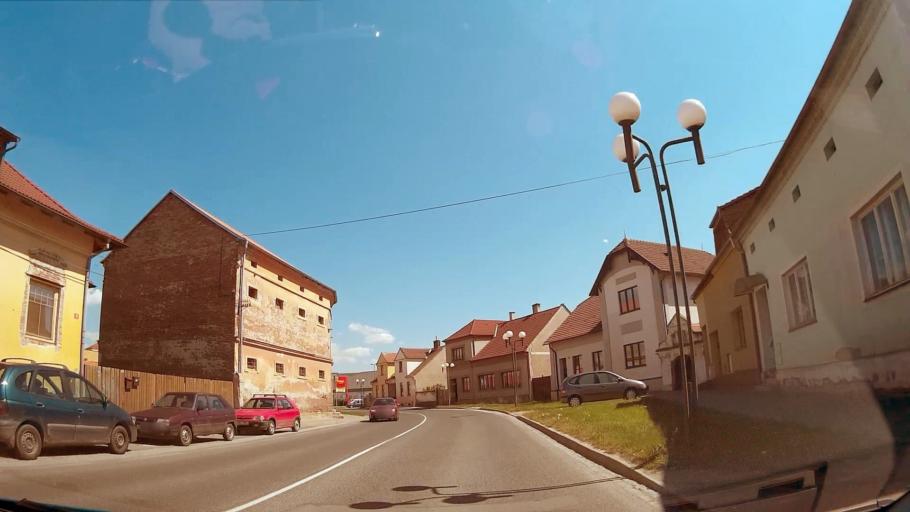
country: CZ
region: South Moravian
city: Ivancice
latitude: 49.0987
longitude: 16.3748
